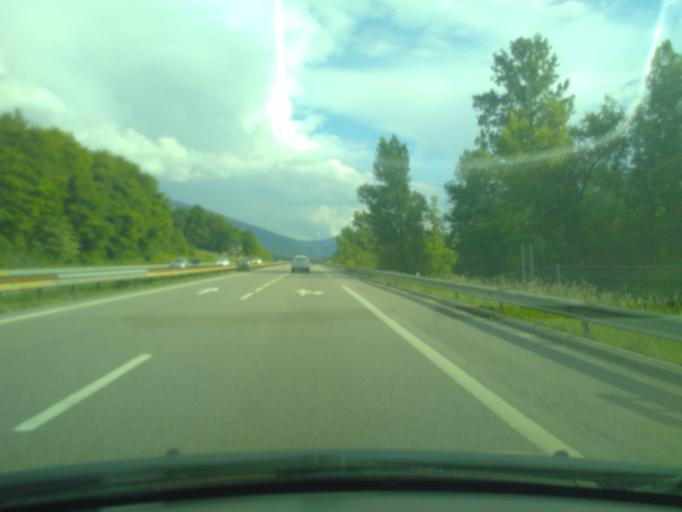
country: FR
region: Rhone-Alpes
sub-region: Departement de la Haute-Savoie
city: Chavanod
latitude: 45.8541
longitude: 6.0564
